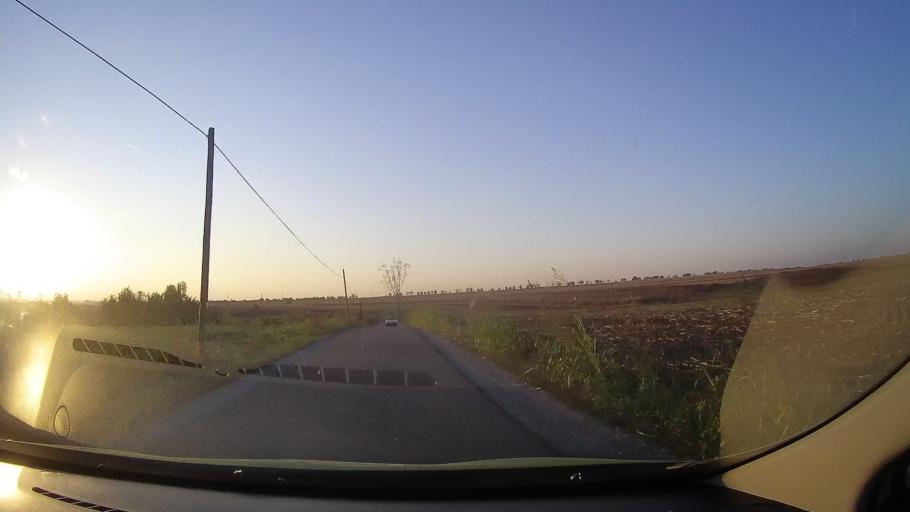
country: RO
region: Bihor
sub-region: Comuna Rosiori
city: Rosiori
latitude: 47.2554
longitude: 21.9831
